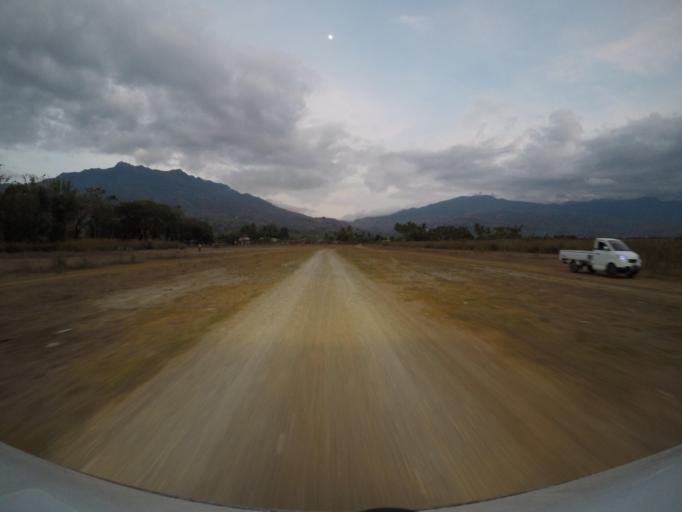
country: TL
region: Bobonaro
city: Maliana
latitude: -8.9734
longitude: 125.2175
